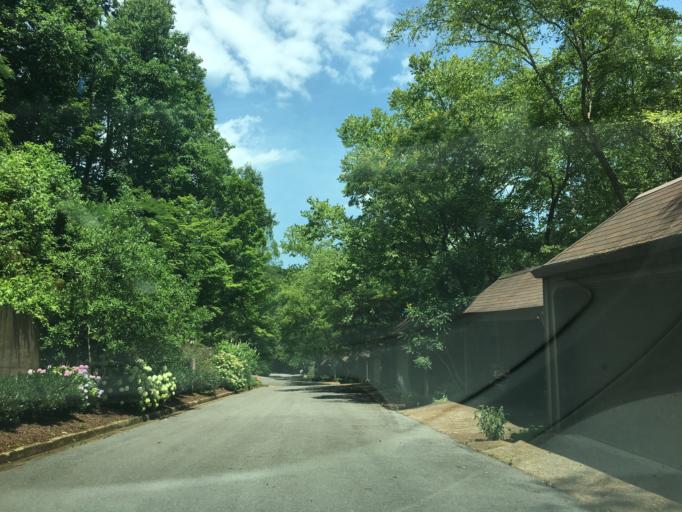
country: US
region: Tennessee
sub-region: Davidson County
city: Belle Meade
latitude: 36.0730
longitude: -86.9143
